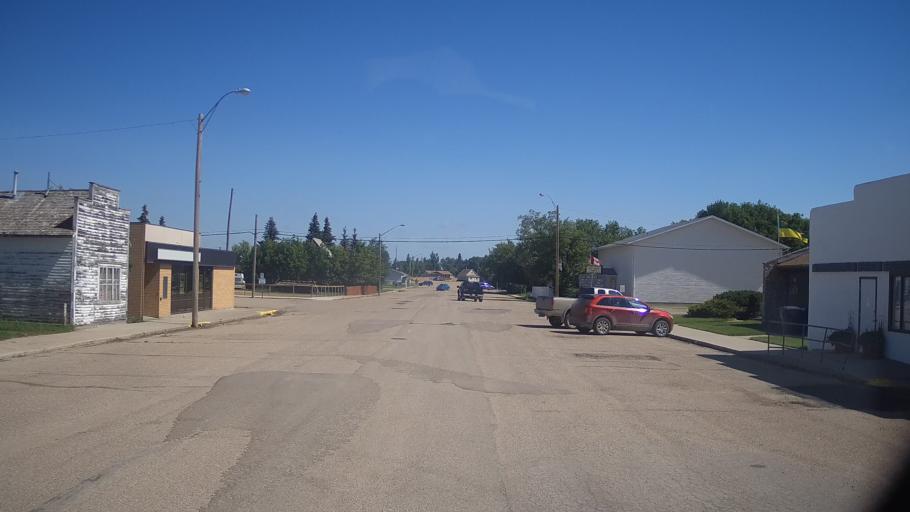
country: CA
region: Saskatchewan
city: Saskatoon
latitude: 51.8935
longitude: -106.0560
